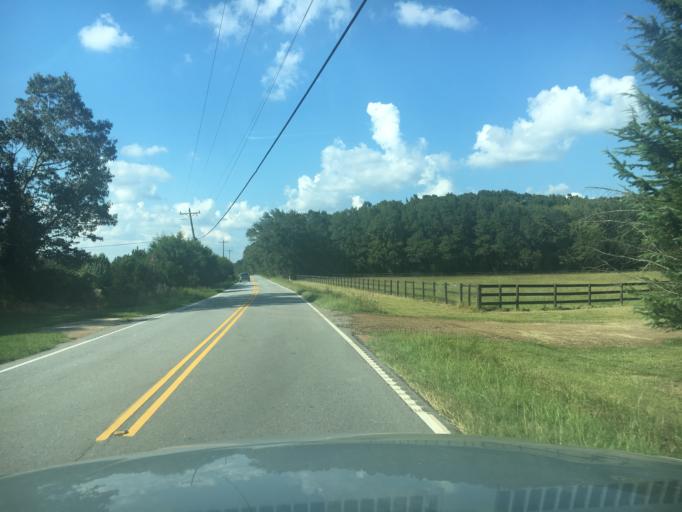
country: US
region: South Carolina
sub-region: Greenville County
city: Fountain Inn
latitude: 34.5861
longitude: -82.2219
